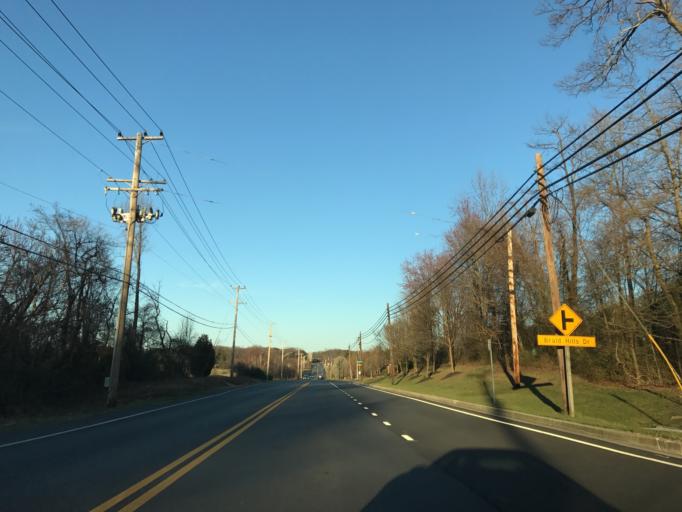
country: US
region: Maryland
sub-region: Anne Arundel County
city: Riviera Beach
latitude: 39.1355
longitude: -76.5041
